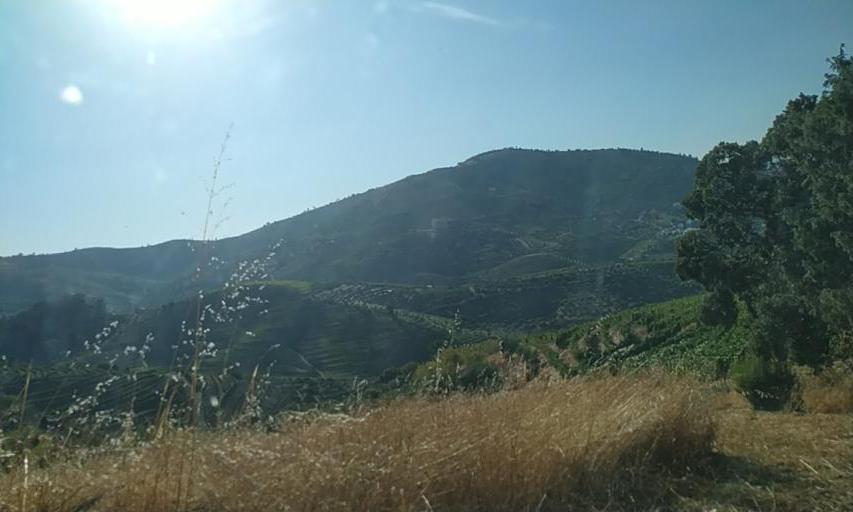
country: PT
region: Viseu
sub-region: Sao Joao da Pesqueira
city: Sao Joao da Pesqueira
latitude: 41.1732
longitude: -7.4068
